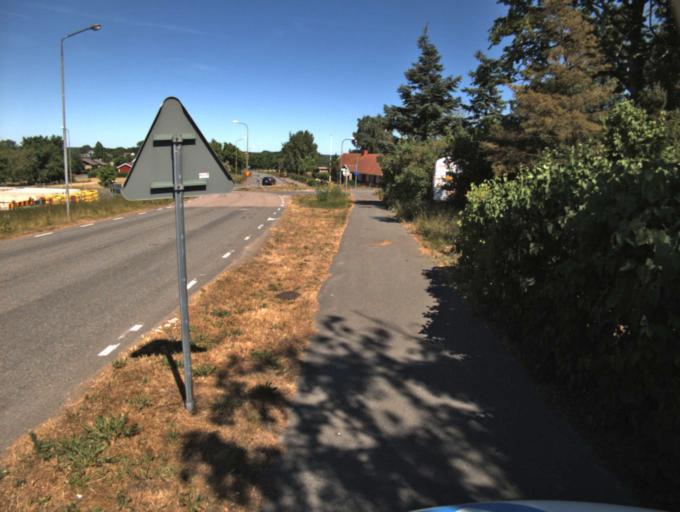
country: SE
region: Skane
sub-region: Kristianstads Kommun
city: Onnestad
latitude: 56.0484
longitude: 14.0211
